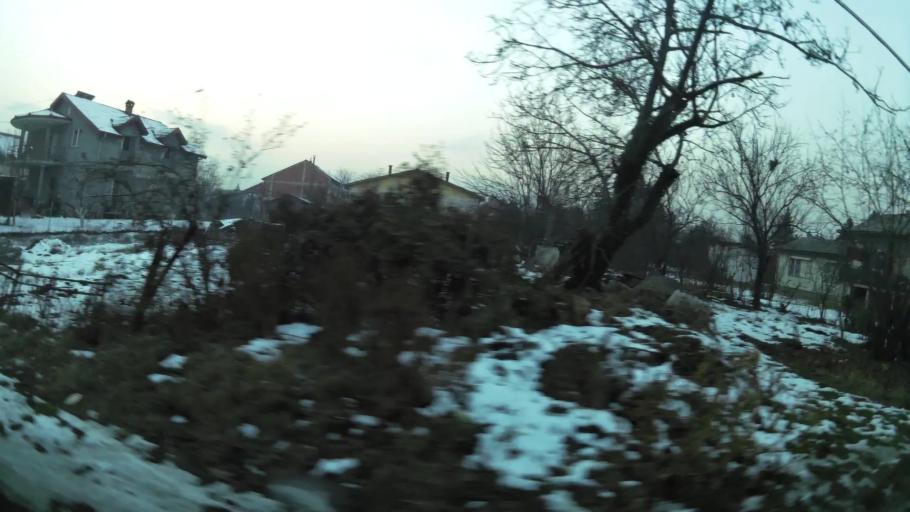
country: MK
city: Creshevo
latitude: 42.0043
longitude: 21.5079
